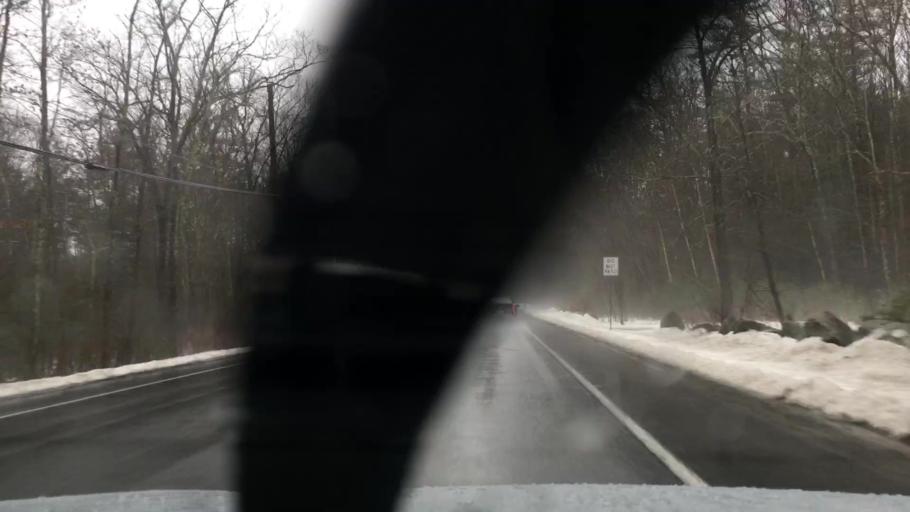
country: US
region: Massachusetts
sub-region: Franklin County
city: Orange
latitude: 42.5444
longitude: -72.2995
